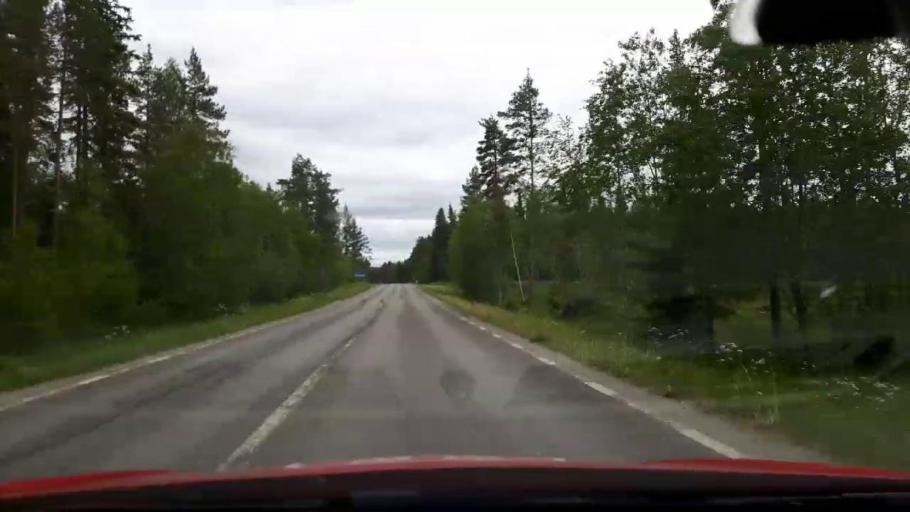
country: SE
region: Jaemtland
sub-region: Ragunda Kommun
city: Hammarstrand
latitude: 63.0864
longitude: 16.3639
